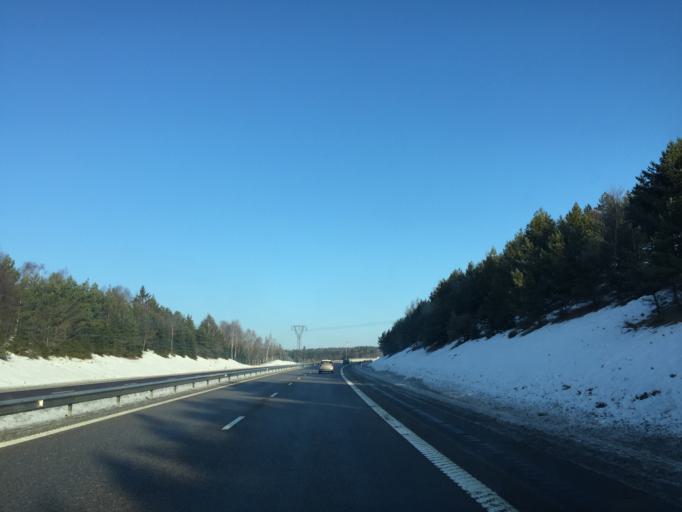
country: SE
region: Vaestra Goetaland
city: Svanesund
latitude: 58.1056
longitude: 11.8799
